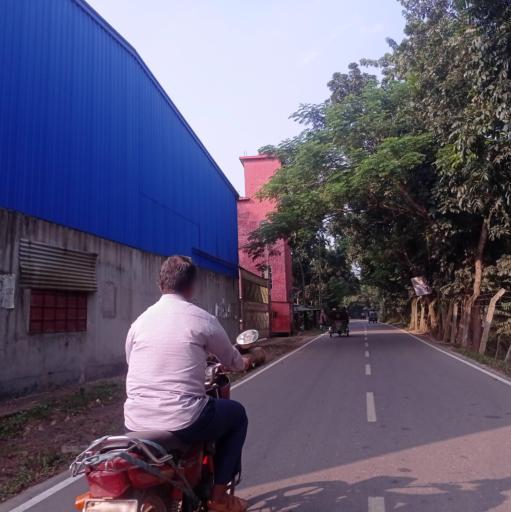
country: BD
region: Dhaka
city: Bhairab Bazar
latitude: 24.0865
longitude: 90.8499
